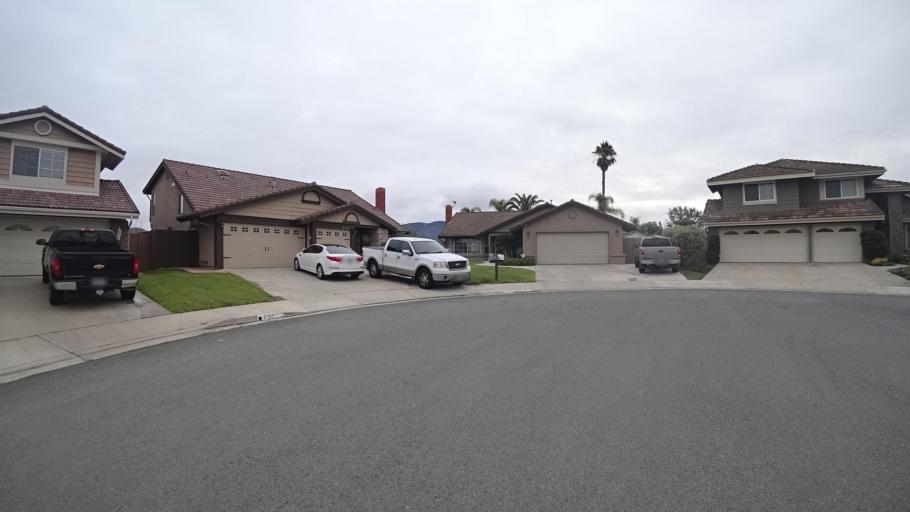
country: US
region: California
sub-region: San Diego County
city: Rancho San Diego
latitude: 32.7555
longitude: -116.9087
